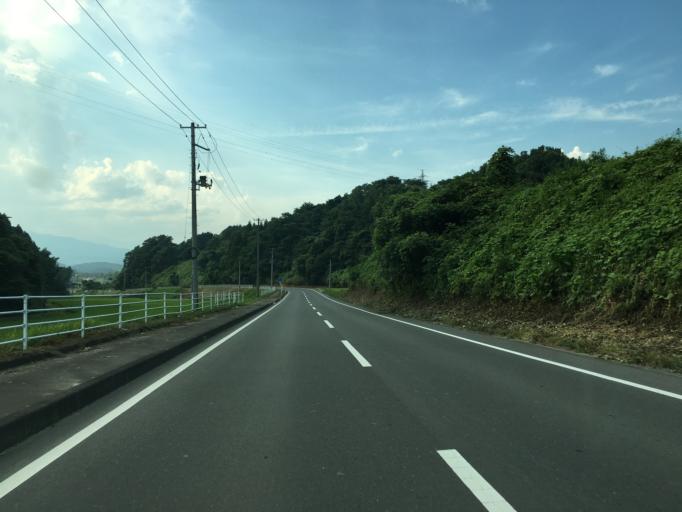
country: JP
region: Fukushima
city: Nihommatsu
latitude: 37.5484
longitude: 140.4416
